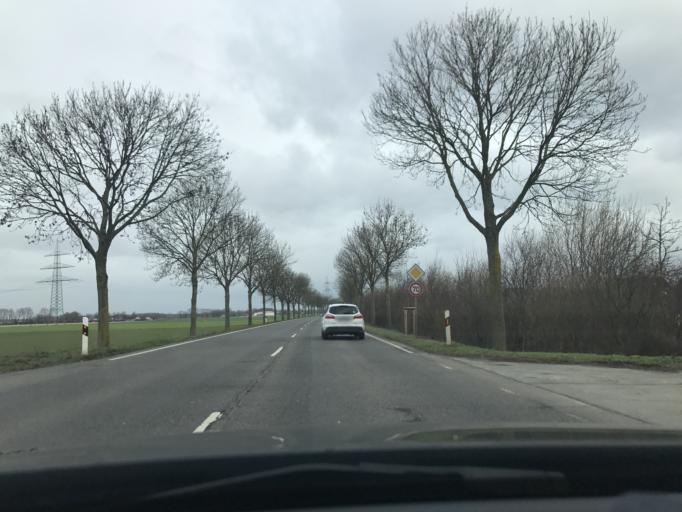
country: DE
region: North Rhine-Westphalia
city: Tonisvorst
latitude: 51.3736
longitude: 6.4911
